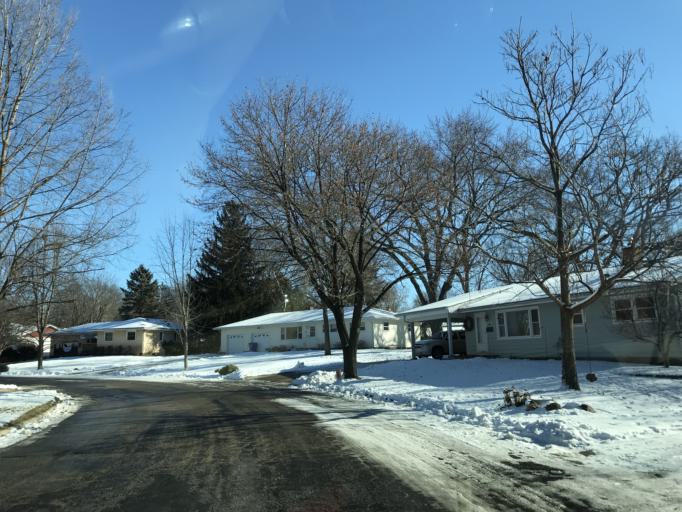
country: US
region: Wisconsin
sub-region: Dane County
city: Monona
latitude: 43.0499
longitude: -89.3310
